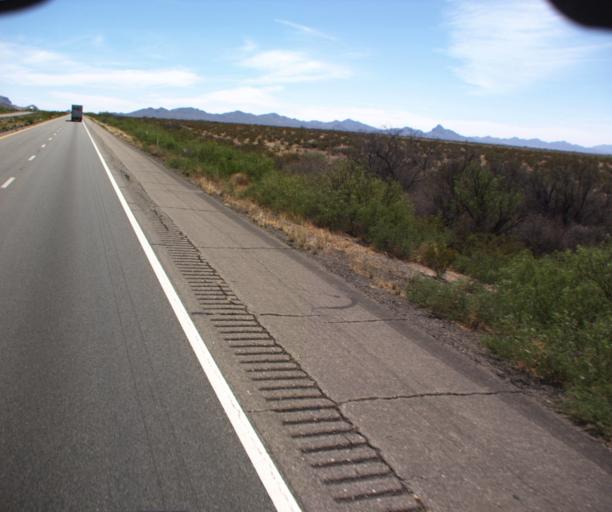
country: US
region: New Mexico
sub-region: Hidalgo County
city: Lordsburg
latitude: 32.2497
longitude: -109.1456
